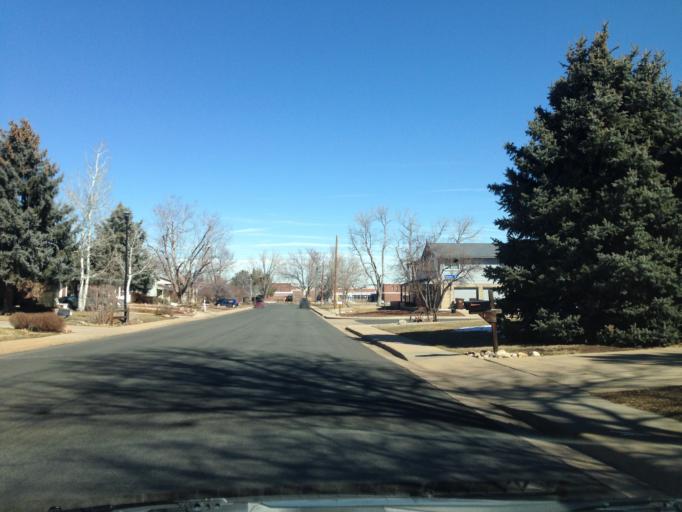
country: US
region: Colorado
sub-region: Boulder County
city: Boulder
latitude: 39.9913
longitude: -105.2290
